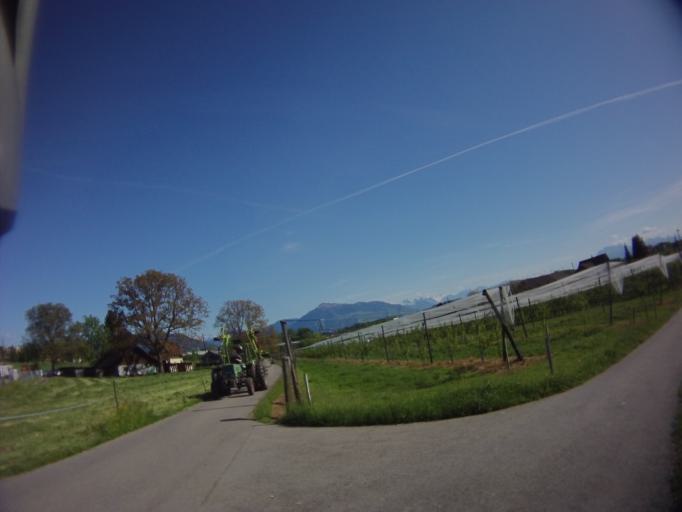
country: CH
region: Zug
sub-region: Zug
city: Cham
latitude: 47.1990
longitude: 8.4490
